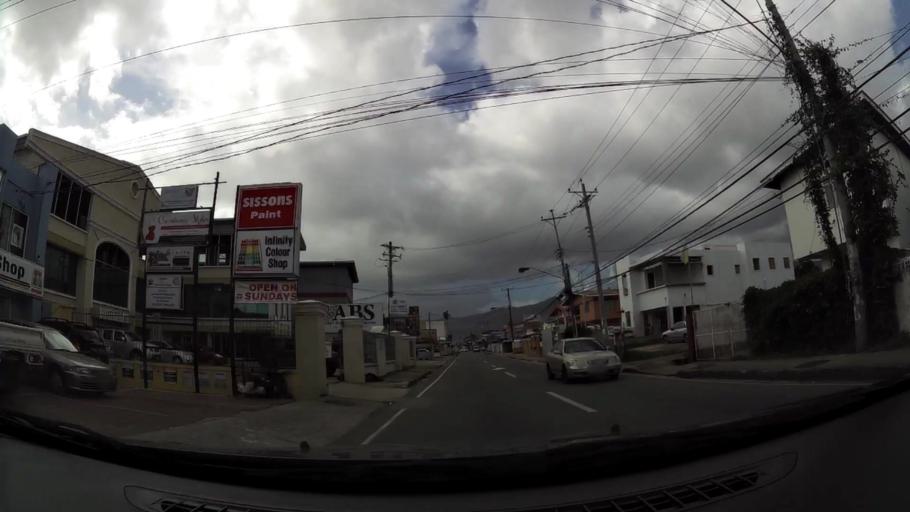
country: TT
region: Tunapuna/Piarco
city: Arouca
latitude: 10.6370
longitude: -61.3461
